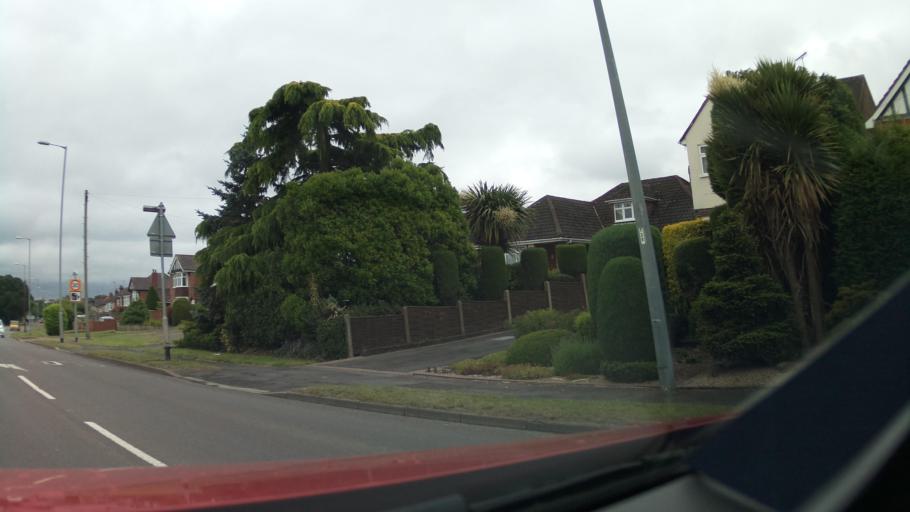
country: GB
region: England
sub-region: Staffordshire
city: Burton upon Trent
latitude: 52.8344
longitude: -1.6541
